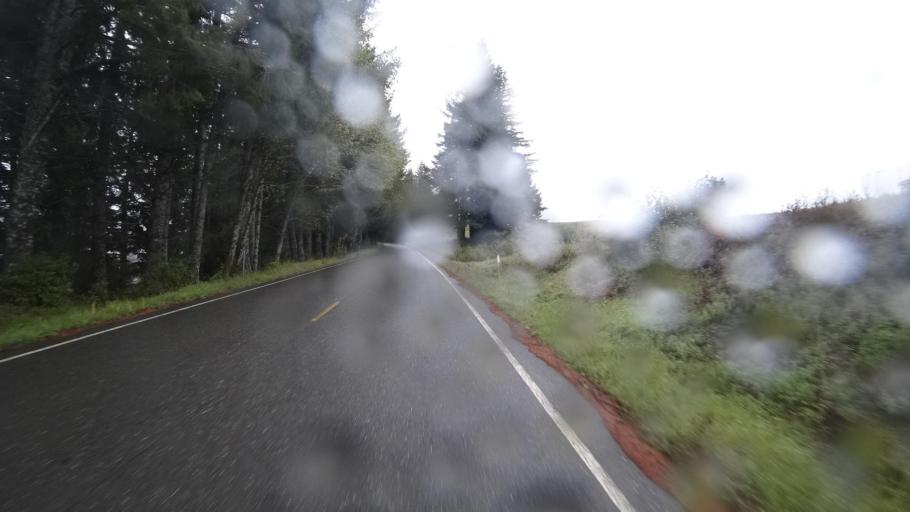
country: US
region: California
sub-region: Humboldt County
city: Westhaven-Moonstone
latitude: 41.1911
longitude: -123.9359
